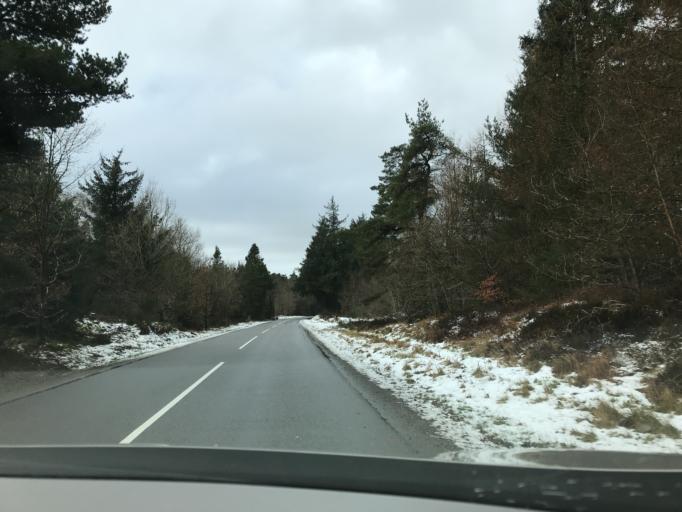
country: DK
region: South Denmark
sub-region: Varde Kommune
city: Oksbol
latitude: 55.7512
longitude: 8.2726
